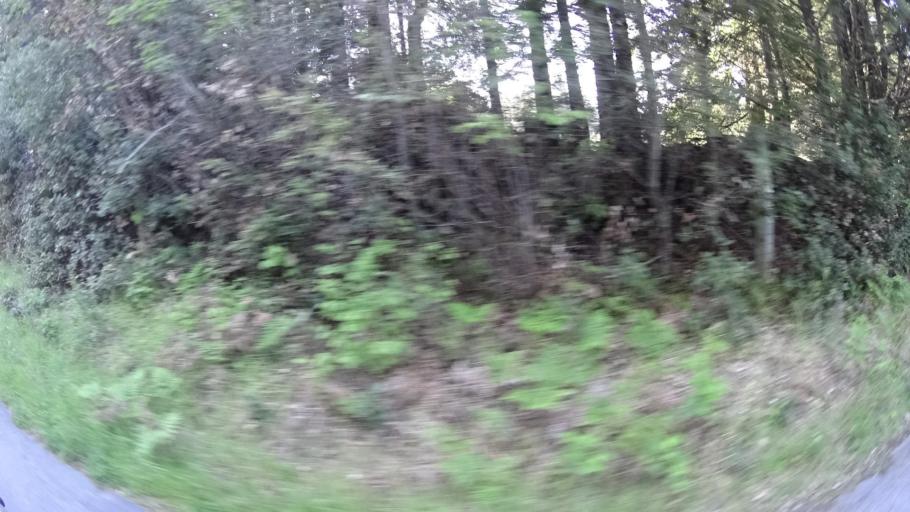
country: US
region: California
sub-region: Humboldt County
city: Rio Dell
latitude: 40.4334
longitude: -123.9690
